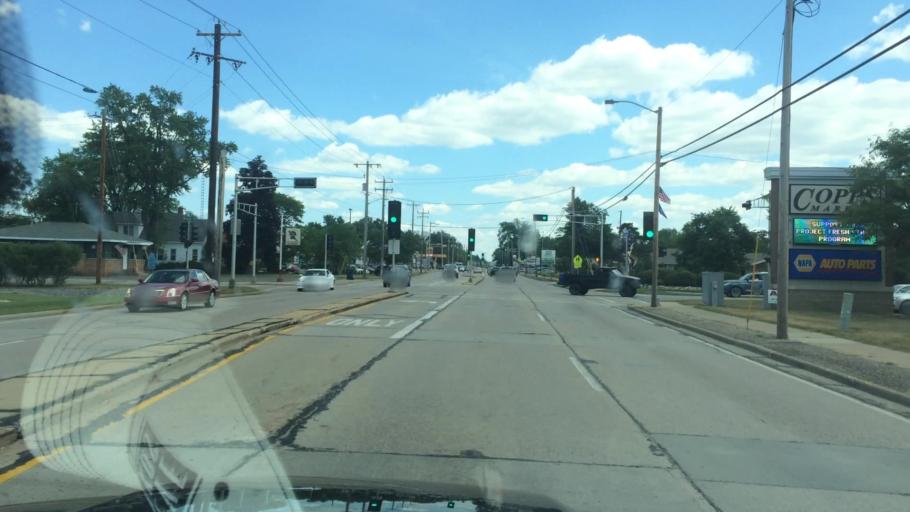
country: US
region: Wisconsin
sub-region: Portage County
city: Stevens Point
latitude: 44.5232
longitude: -89.5508
